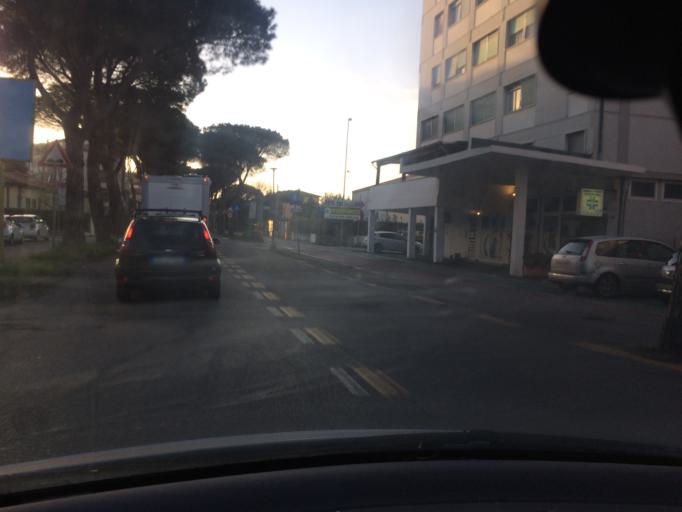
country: IT
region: Tuscany
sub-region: Province of Pisa
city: Pisa
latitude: 43.7215
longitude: 10.4187
